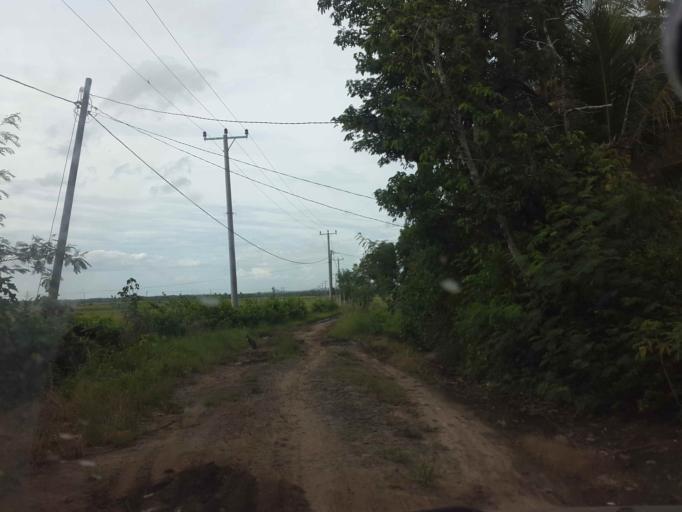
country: ID
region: Lampung
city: Jabung
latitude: -5.5067
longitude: 105.6309
